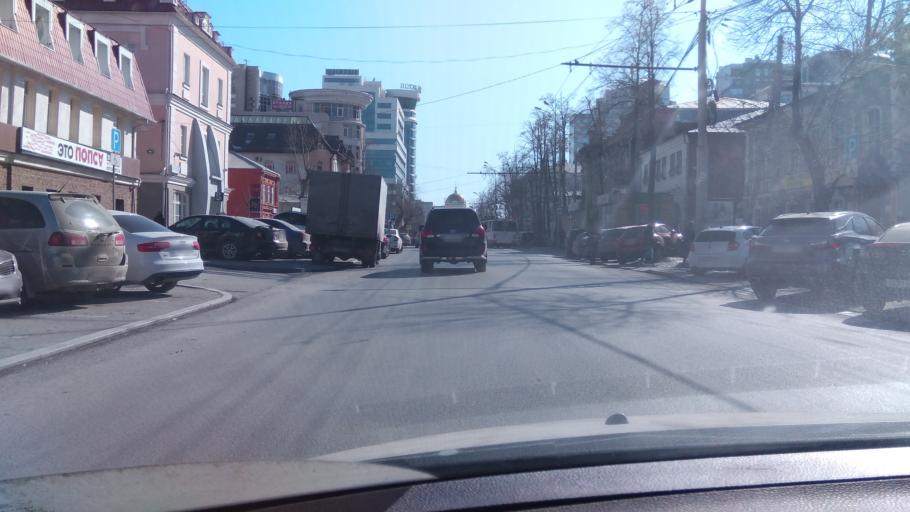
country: RU
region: Sverdlovsk
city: Yekaterinburg
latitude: 56.8323
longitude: 60.6130
